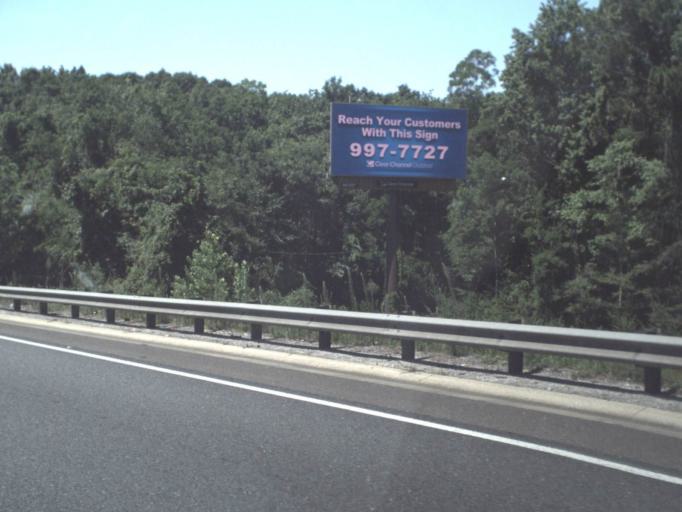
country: US
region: Florida
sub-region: Duval County
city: Jacksonville
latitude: 30.3200
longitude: -81.7706
